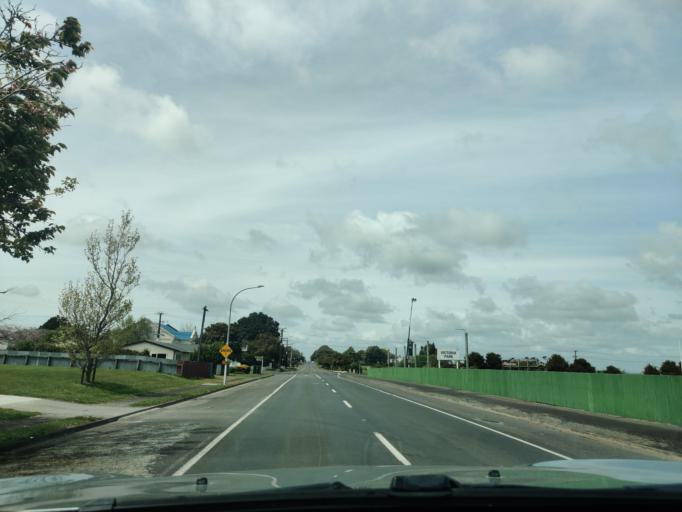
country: NZ
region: Taranaki
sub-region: South Taranaki District
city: Eltham
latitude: -39.4290
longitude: 174.1519
